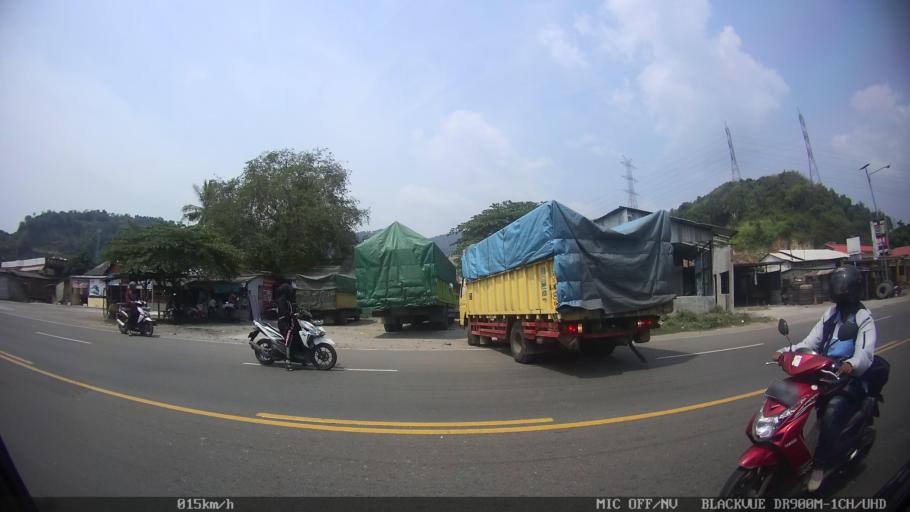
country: ID
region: Banten
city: Curug
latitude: -5.9569
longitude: 106.0044
